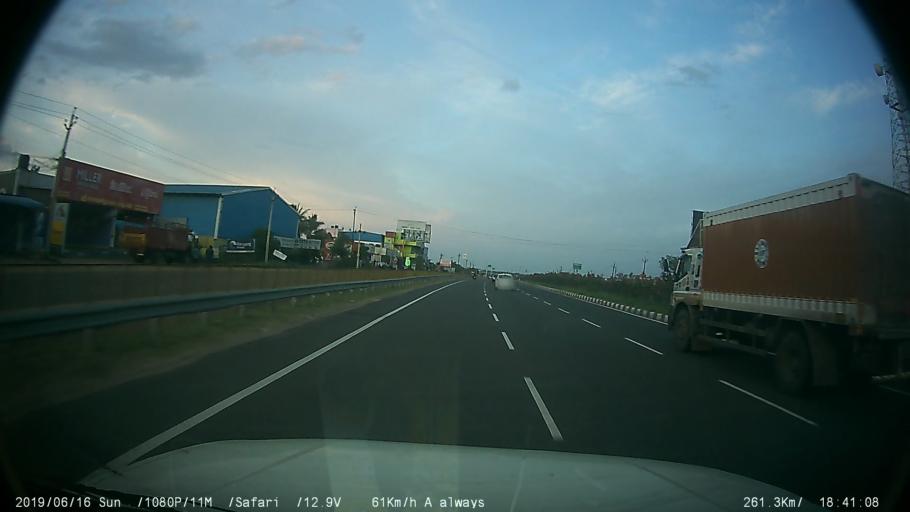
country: IN
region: Tamil Nadu
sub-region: Coimbatore
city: Sulur
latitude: 11.0916
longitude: 77.1397
